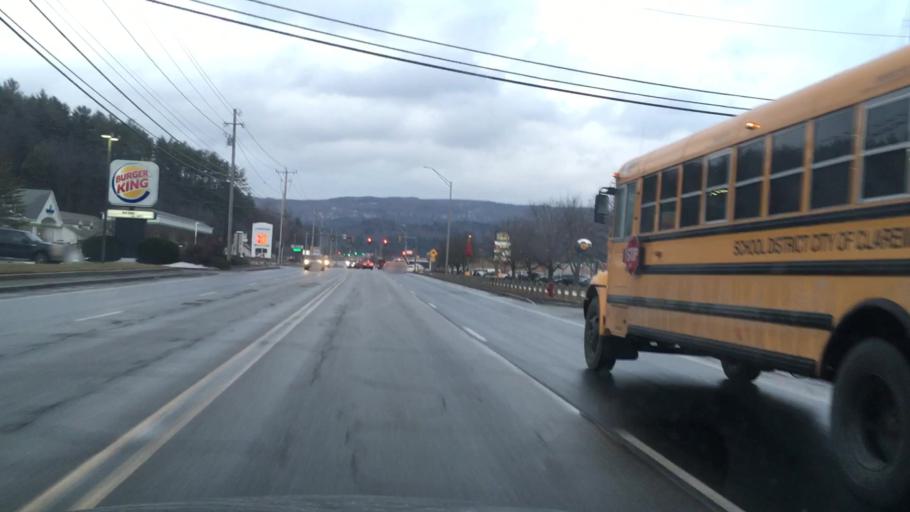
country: US
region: New Hampshire
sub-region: Sullivan County
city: Claremont
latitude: 43.3657
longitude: -72.3206
